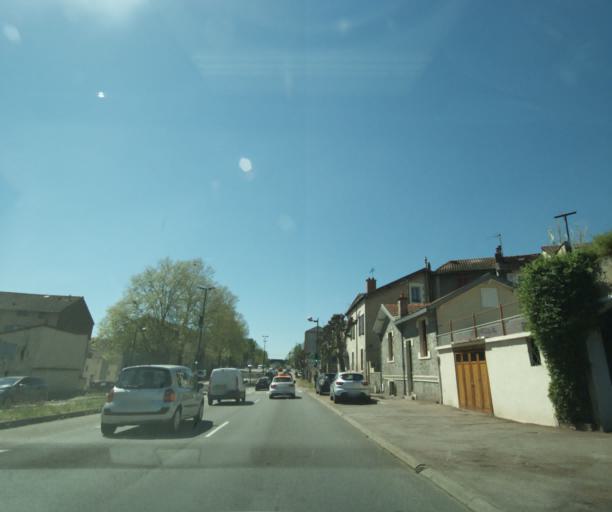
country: FR
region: Limousin
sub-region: Departement de la Haute-Vienne
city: Limoges
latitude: 45.8222
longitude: 1.2646
